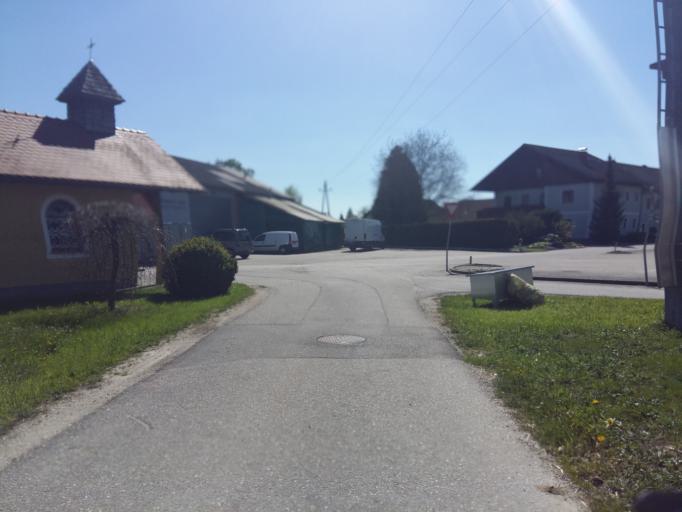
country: AT
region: Upper Austria
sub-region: Politischer Bezirk Scharding
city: Sankt Marienkirchen bei Schaerding
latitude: 48.3944
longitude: 13.4485
